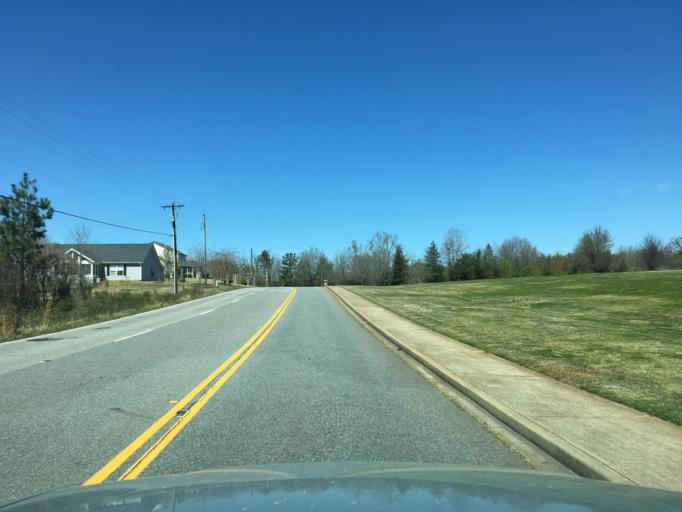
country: US
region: South Carolina
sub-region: Spartanburg County
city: Roebuck
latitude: 34.8828
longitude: -82.0054
